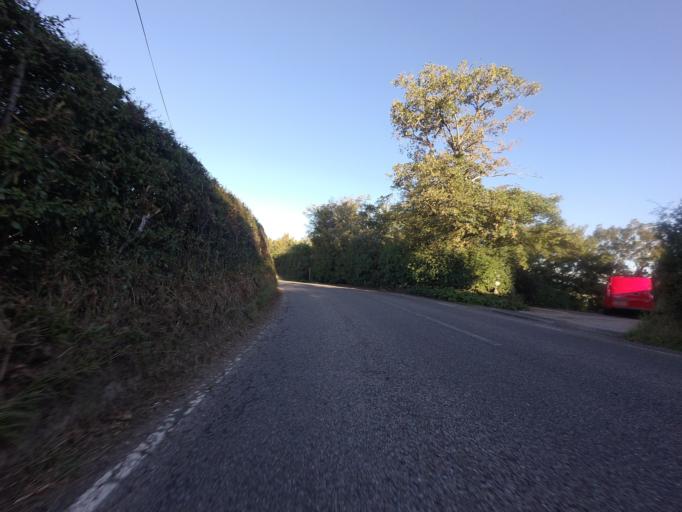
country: GB
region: England
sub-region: Kent
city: Sturry
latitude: 51.3247
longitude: 1.2028
